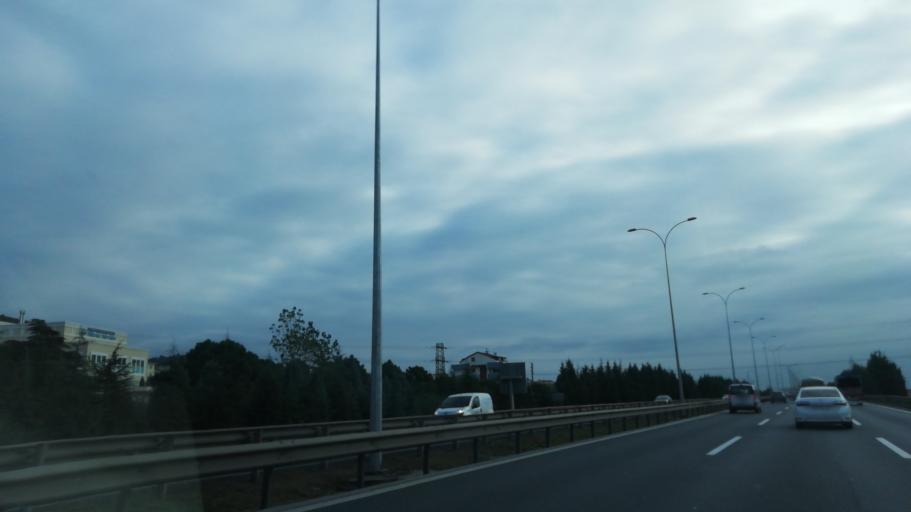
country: TR
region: Kocaeli
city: Korfez
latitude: 40.7732
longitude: 29.7662
